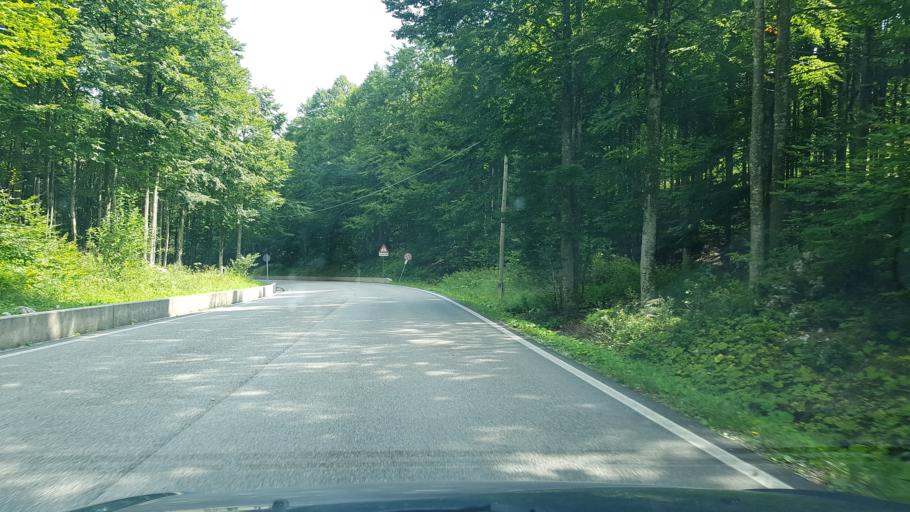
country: IT
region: Friuli Venezia Giulia
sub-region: Provincia di Pordenone
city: Budoia
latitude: 46.1056
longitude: 12.5231
